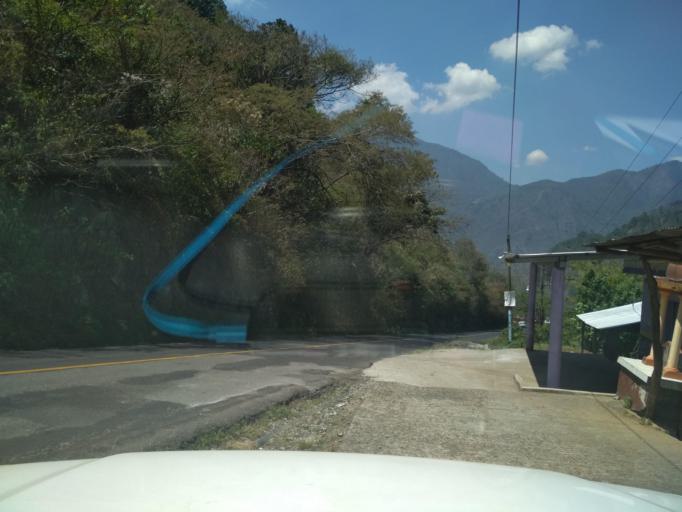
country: MX
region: Veracruz
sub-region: Tlilapan
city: Tonalixco
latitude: 18.7831
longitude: -97.0852
